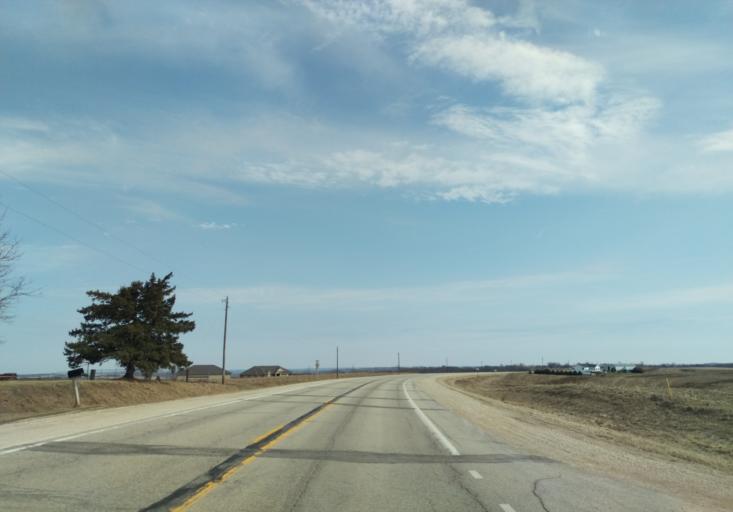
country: US
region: Iowa
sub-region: Clayton County
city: Monona
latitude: 43.1841
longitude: -91.3292
